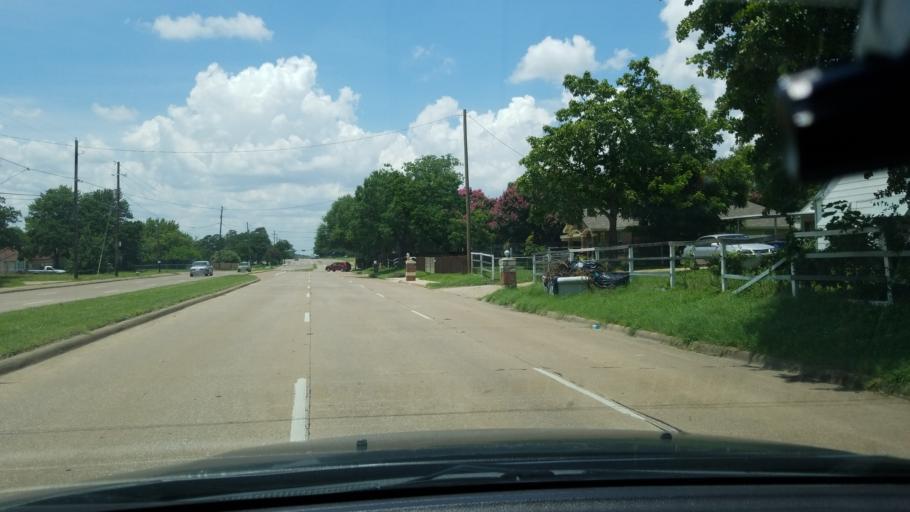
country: US
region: Texas
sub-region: Dallas County
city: Balch Springs
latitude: 32.7487
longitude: -96.6449
